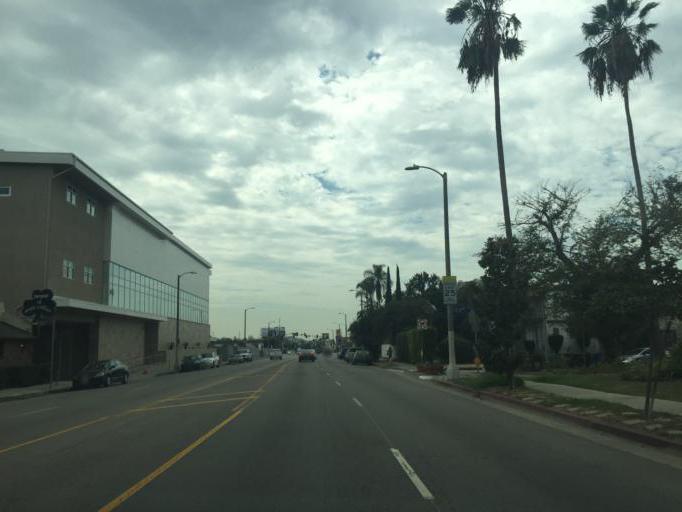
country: US
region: California
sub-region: Los Angeles County
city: West Hollywood
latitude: 34.0605
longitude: -118.3627
